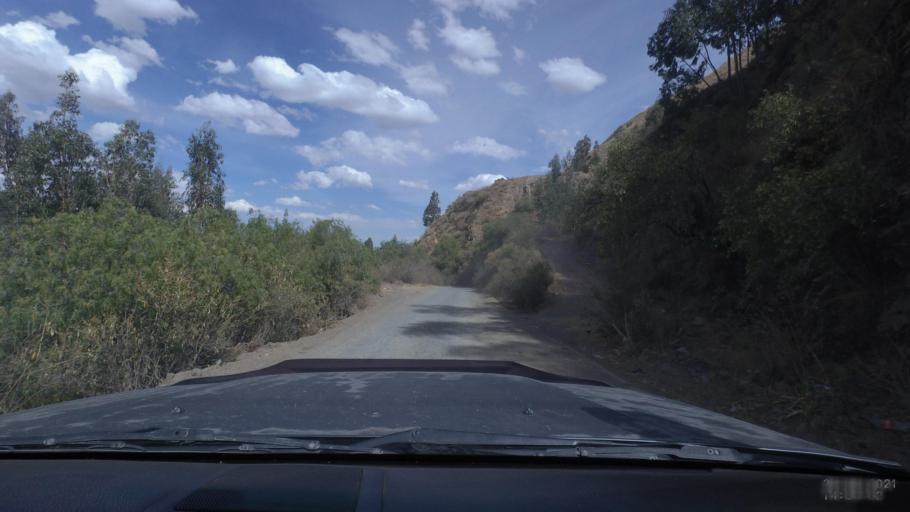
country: BO
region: Cochabamba
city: Cochabamba
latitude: -17.2872
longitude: -66.3039
